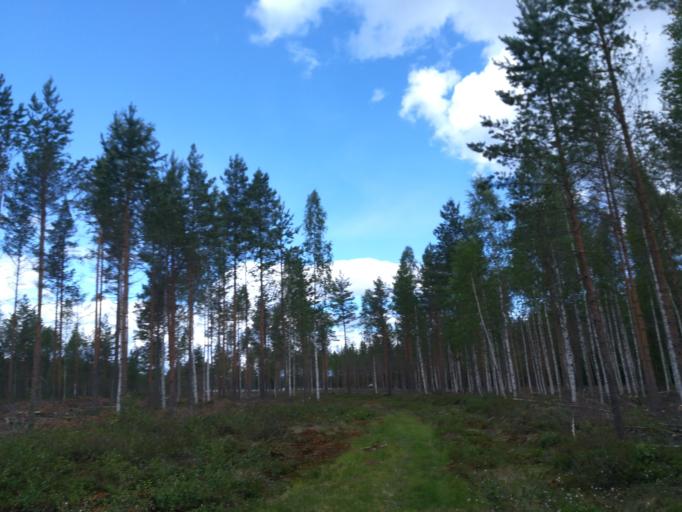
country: FI
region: Southern Savonia
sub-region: Mikkeli
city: Hirvensalmi
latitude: 61.6545
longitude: 26.7812
